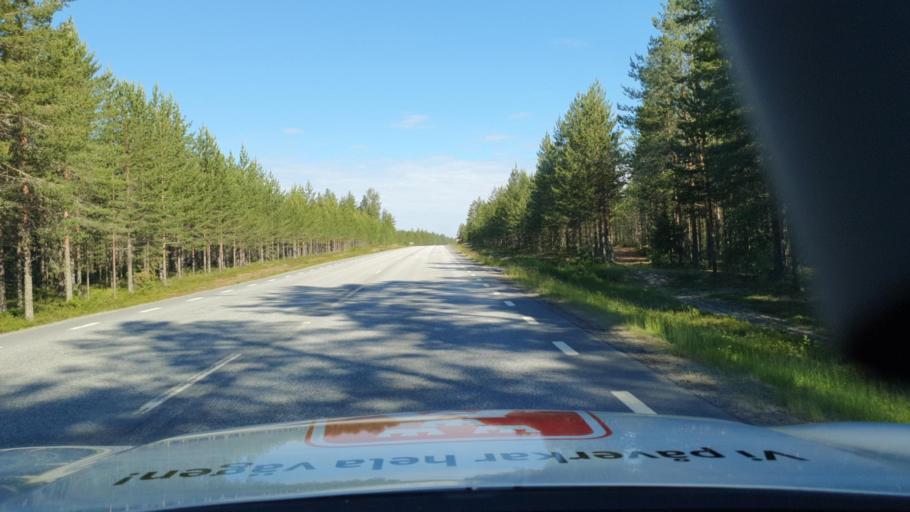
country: SE
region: Vaesterbotten
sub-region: Vannas Kommun
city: Vannasby
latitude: 64.0314
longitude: 20.0163
